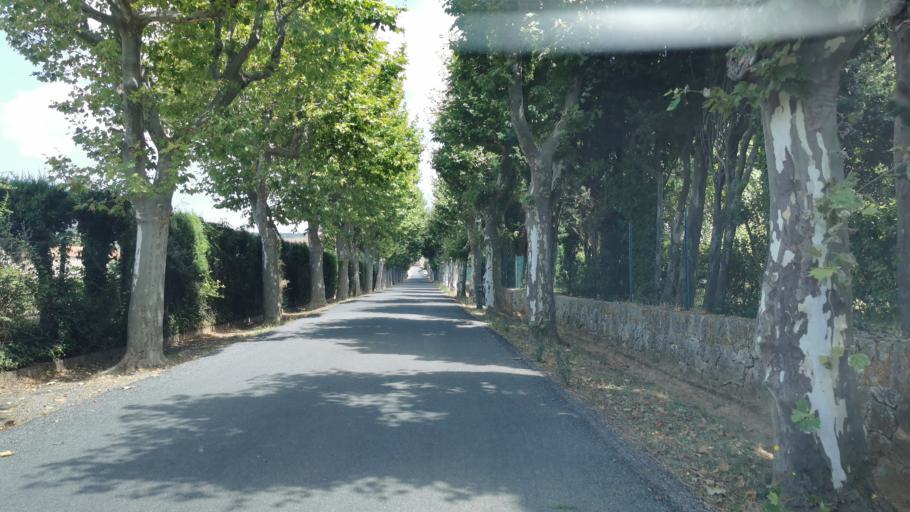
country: FR
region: Languedoc-Roussillon
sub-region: Departement de l'Aude
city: Bizanet
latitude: 43.1606
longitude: 2.8675
